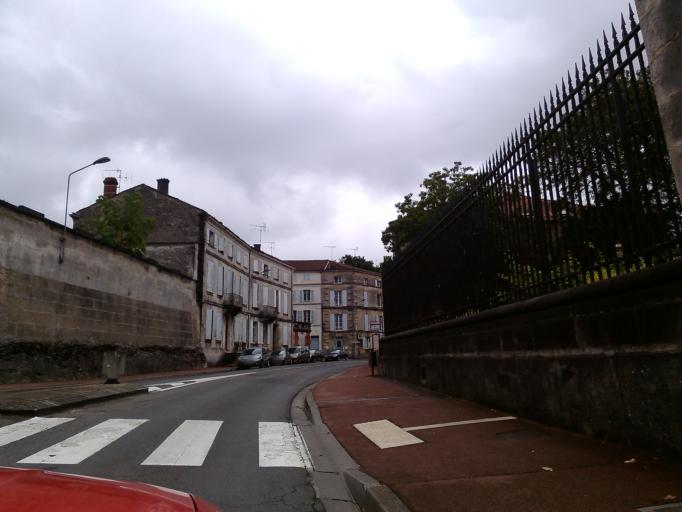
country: FR
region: Poitou-Charentes
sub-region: Departement de la Charente
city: Cognac
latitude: 45.6985
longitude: -0.3285
